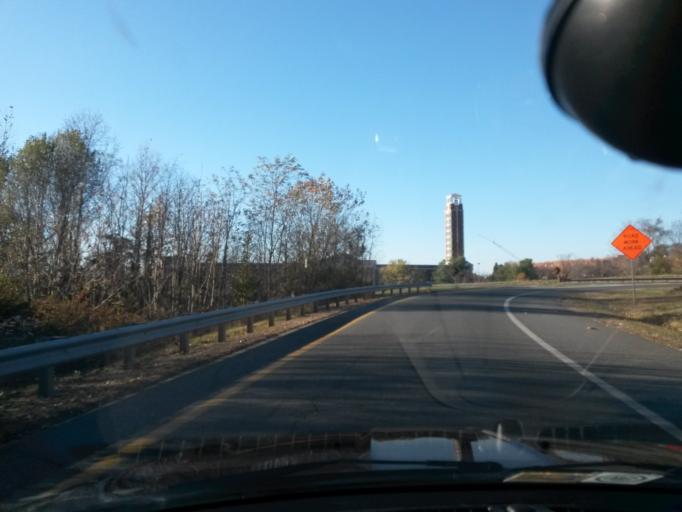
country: US
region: Virginia
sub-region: City of Lynchburg
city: West Lynchburg
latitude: 37.3489
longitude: -79.1770
